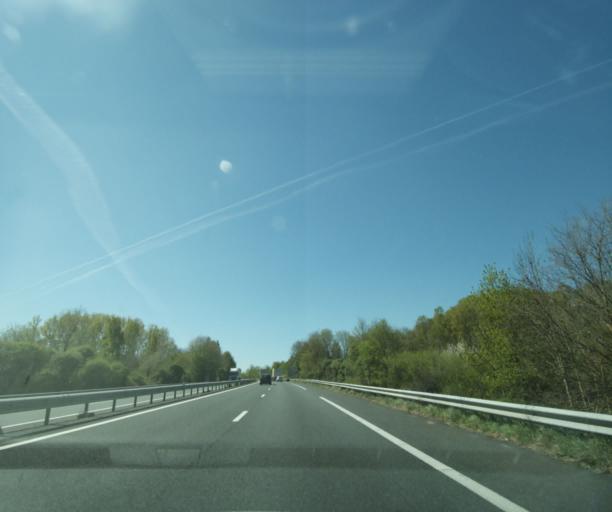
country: FR
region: Centre
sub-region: Departement de l'Indre
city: Chantome
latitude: 46.4525
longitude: 1.4931
